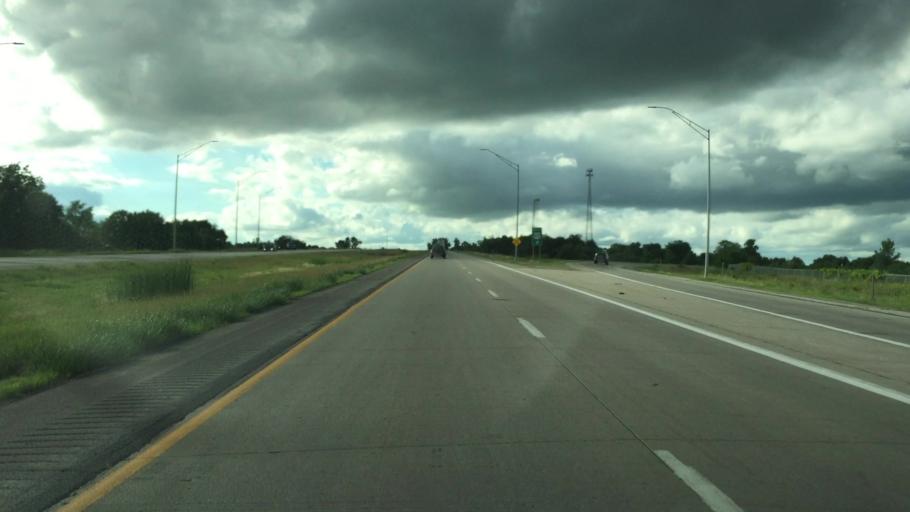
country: US
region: Iowa
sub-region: Polk County
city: Altoona
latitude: 41.6555
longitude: -93.5182
